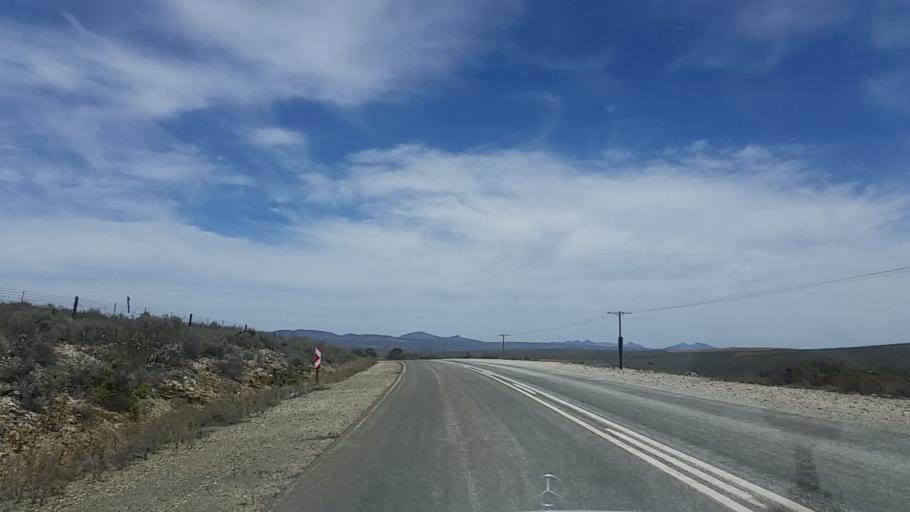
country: ZA
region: Eastern Cape
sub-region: Cacadu District Municipality
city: Willowmore
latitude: -33.5904
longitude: 23.1536
